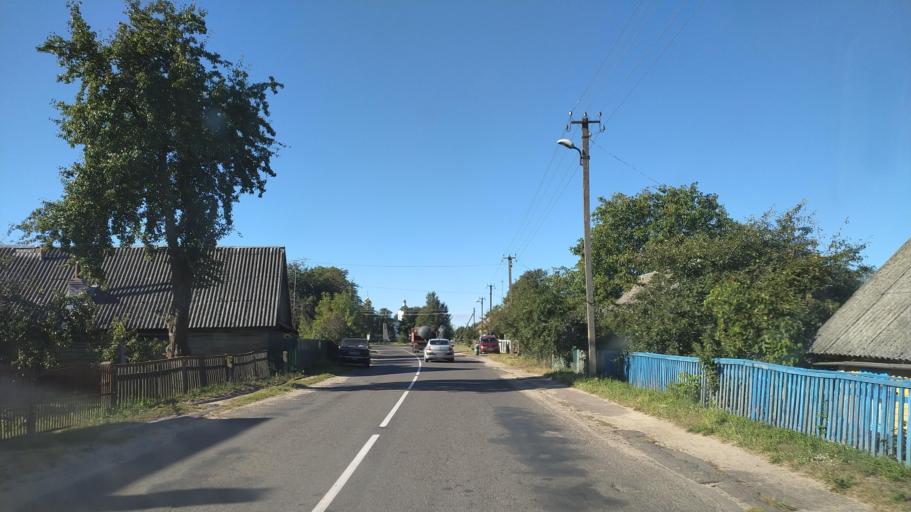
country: BY
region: Brest
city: Pruzhany
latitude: 52.4840
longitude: 24.7061
